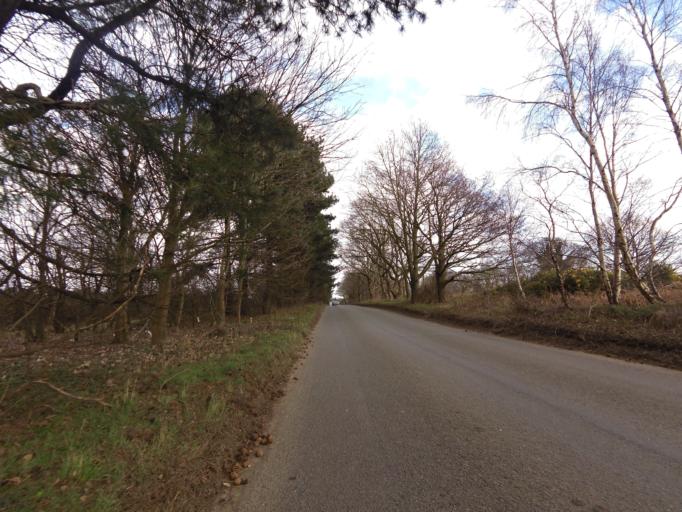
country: GB
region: England
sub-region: Suffolk
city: Woodbridge
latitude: 52.0533
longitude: 1.2978
